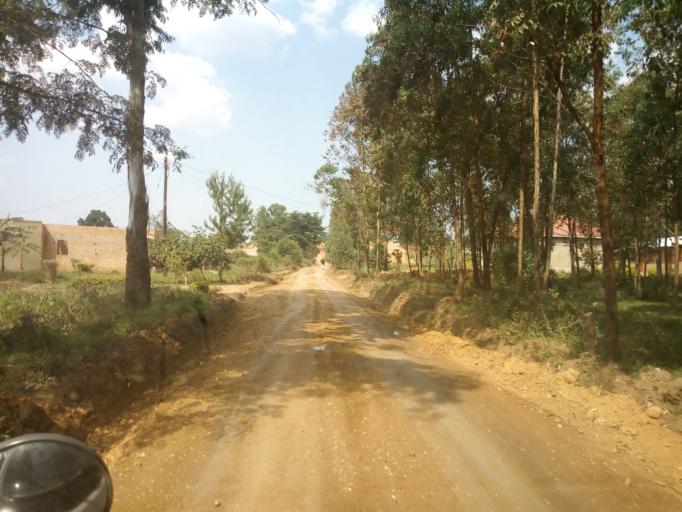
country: UG
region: Western Region
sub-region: Kanungu District
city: Ntungamo
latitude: -0.7837
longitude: 29.6977
